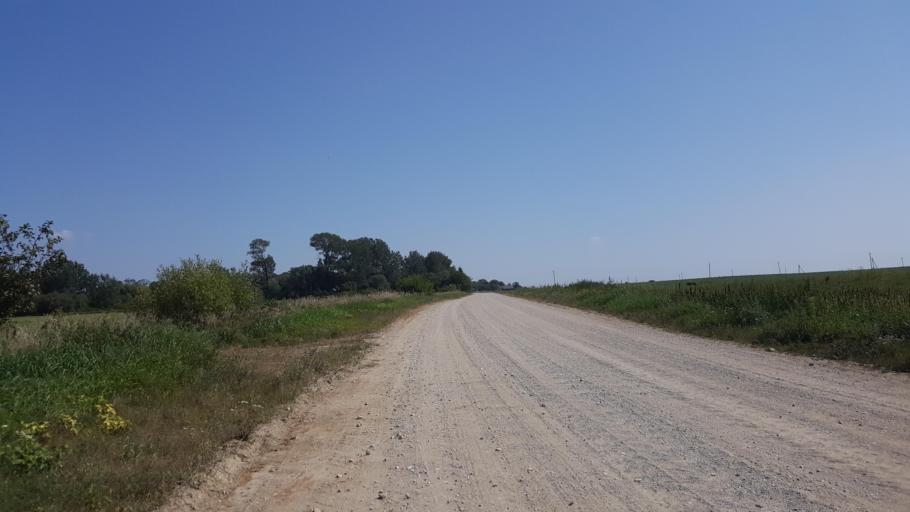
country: PL
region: Podlasie
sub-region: Powiat hajnowski
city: Czeremcha
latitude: 52.4681
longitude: 23.4718
